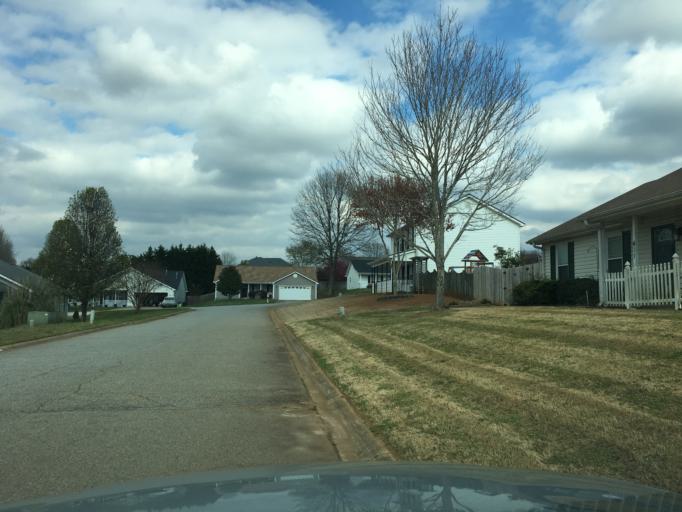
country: US
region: South Carolina
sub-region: Spartanburg County
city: Duncan
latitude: 34.8930
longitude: -82.1326
